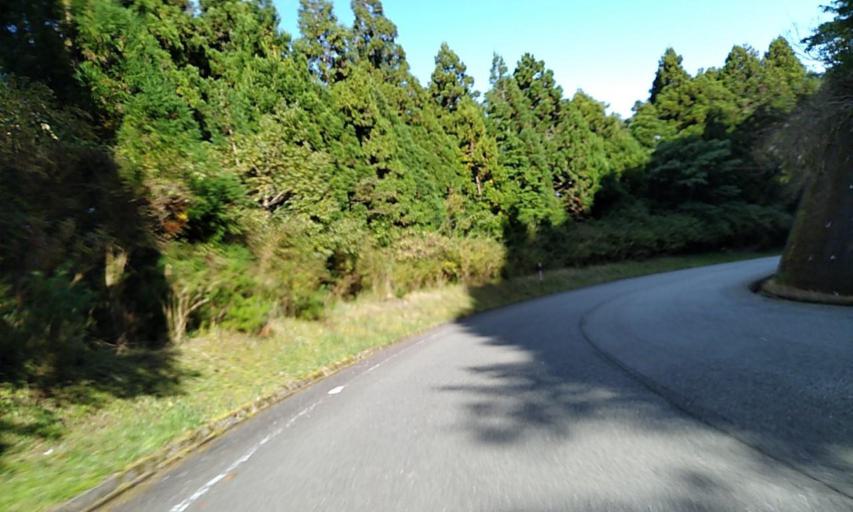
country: JP
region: Wakayama
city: Kainan
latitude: 34.1089
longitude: 135.3316
